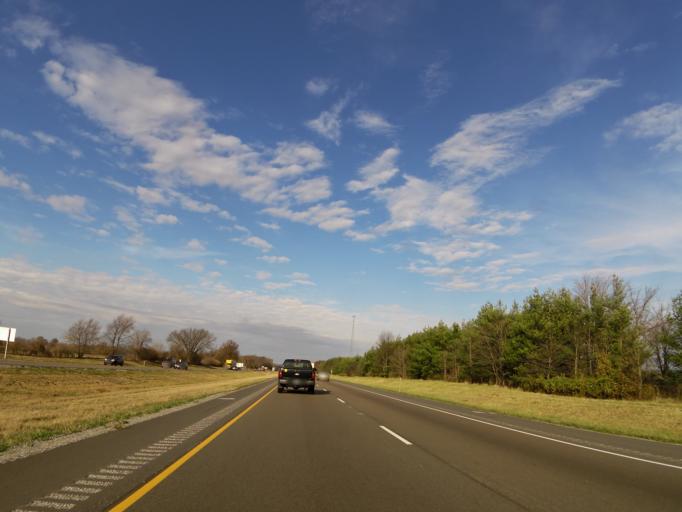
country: US
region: Illinois
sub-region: Washington County
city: Okawville
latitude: 38.4515
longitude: -89.5522
